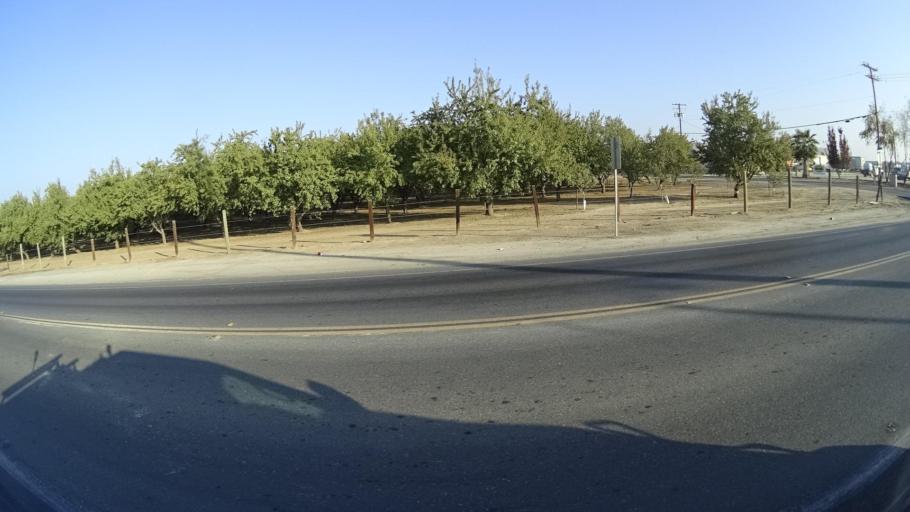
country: US
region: California
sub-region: Kern County
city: Delano
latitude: 35.7904
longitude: -119.2328
